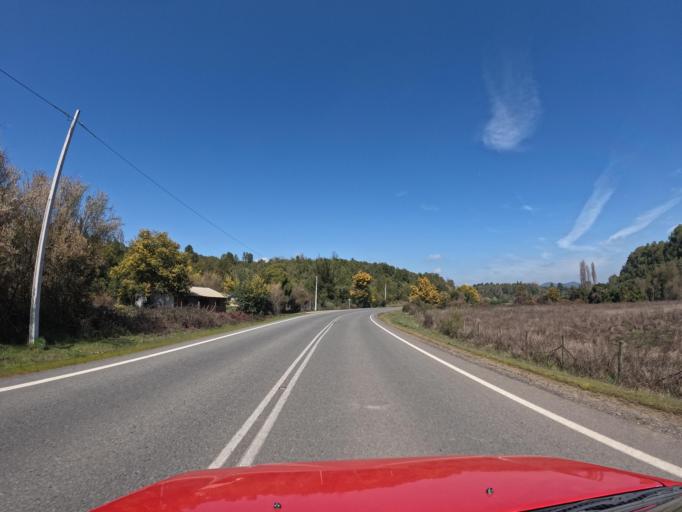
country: CL
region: Maule
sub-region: Provincia de Talca
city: San Clemente
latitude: -35.4622
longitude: -71.2696
